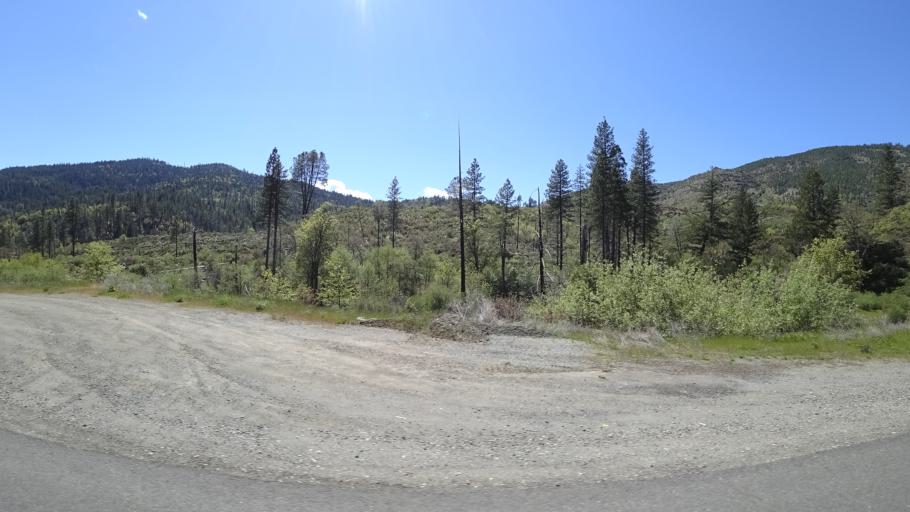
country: US
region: California
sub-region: Trinity County
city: Weaverville
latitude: 40.7421
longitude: -122.9679
